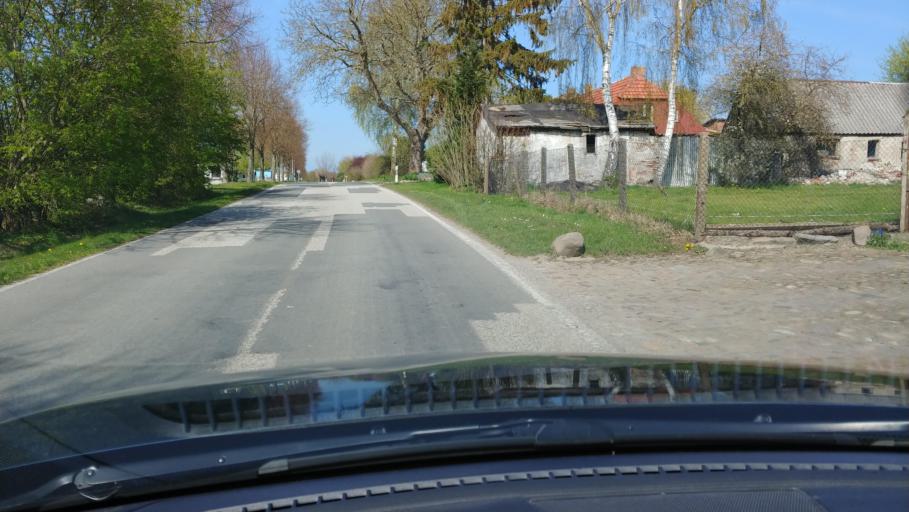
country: DE
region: Mecklenburg-Vorpommern
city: Muhlen Eichsen
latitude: 53.7834
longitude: 11.2662
